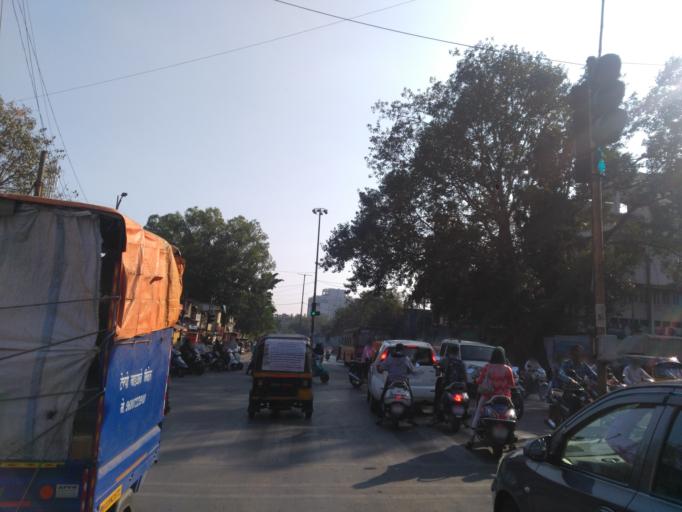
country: IN
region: Maharashtra
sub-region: Pune Division
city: Pune
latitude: 18.4968
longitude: 73.8693
